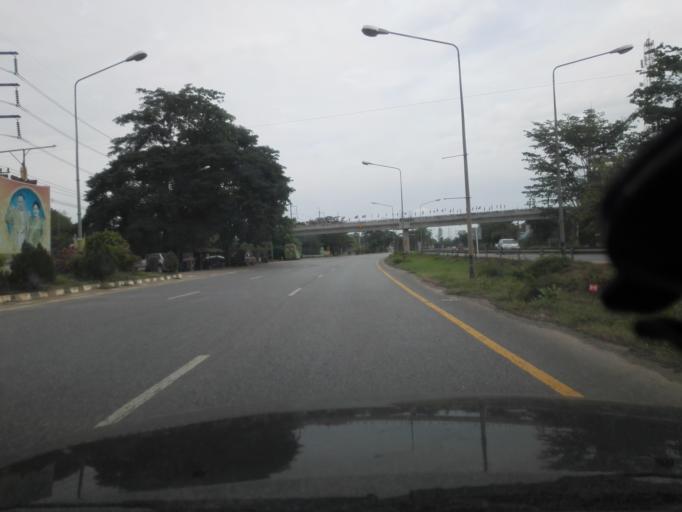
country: TH
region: Kamphaeng Phet
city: Khlong Khlung
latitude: 16.1026
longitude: 99.7195
